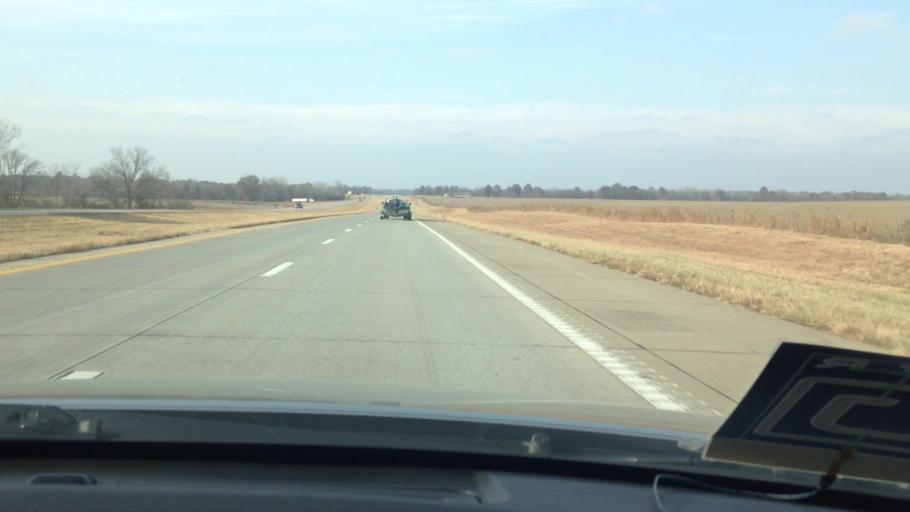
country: US
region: Missouri
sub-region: Henry County
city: Clinton
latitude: 38.4462
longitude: -93.9564
